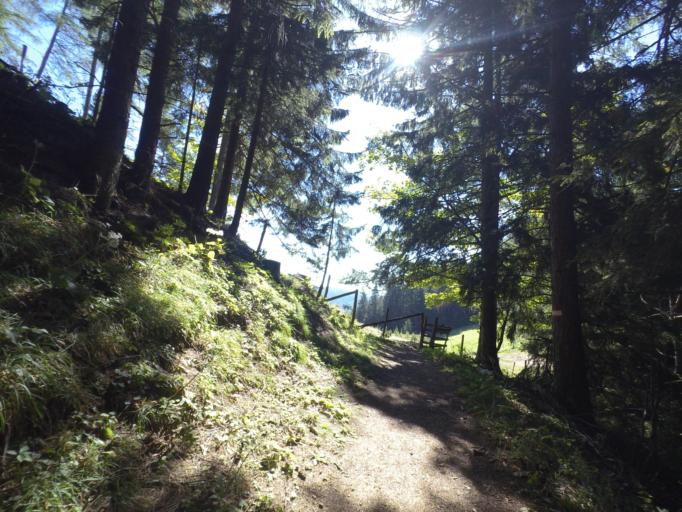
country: AT
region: Styria
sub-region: Politischer Bezirk Weiz
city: Passail
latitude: 47.3316
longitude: 15.4640
